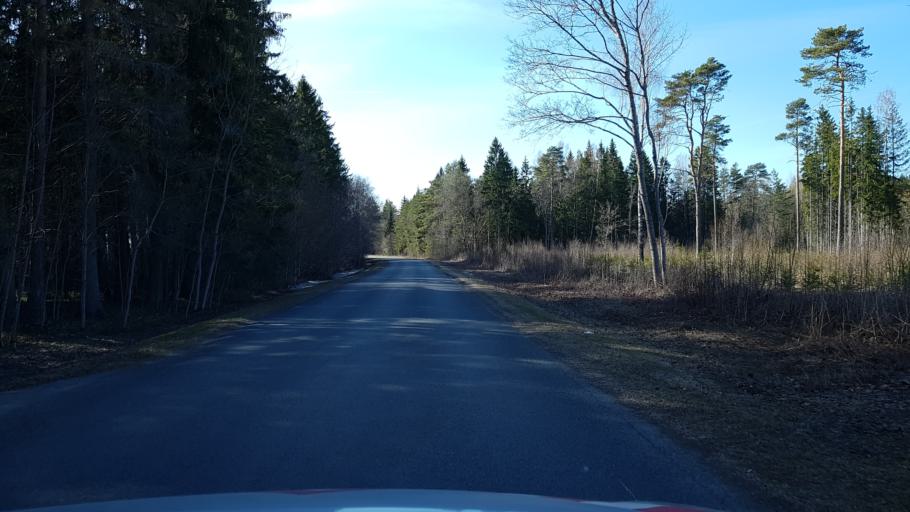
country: EE
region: Harju
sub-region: Nissi vald
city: Riisipere
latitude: 59.0982
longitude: 24.3318
